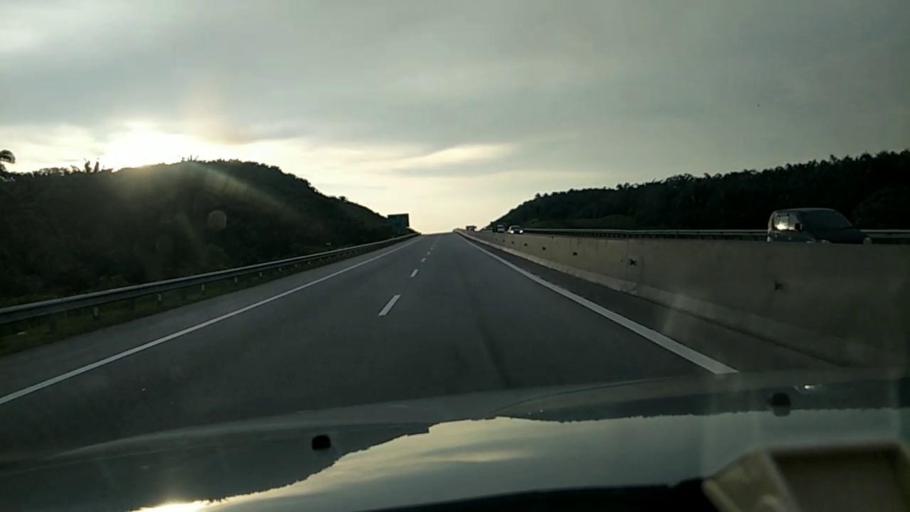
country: MY
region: Selangor
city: Batu Arang
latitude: 3.2807
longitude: 101.4475
